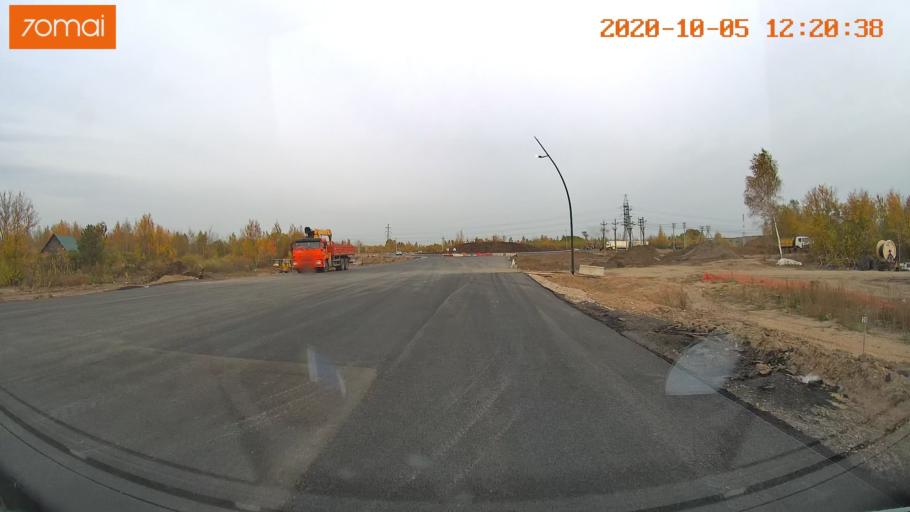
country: RU
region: Ivanovo
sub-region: Gorod Ivanovo
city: Ivanovo
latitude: 56.9651
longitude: 40.9311
